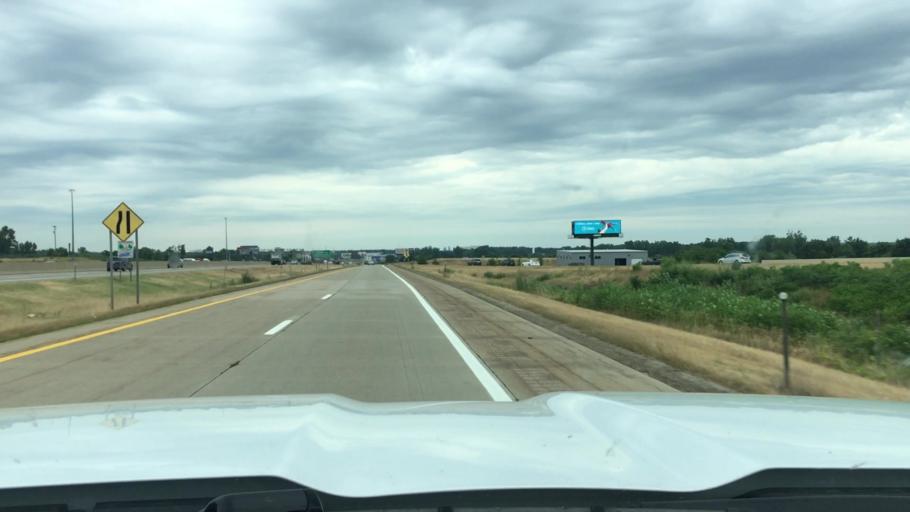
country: US
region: Michigan
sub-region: Kent County
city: Cutlerville
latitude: 42.8512
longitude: -85.6782
